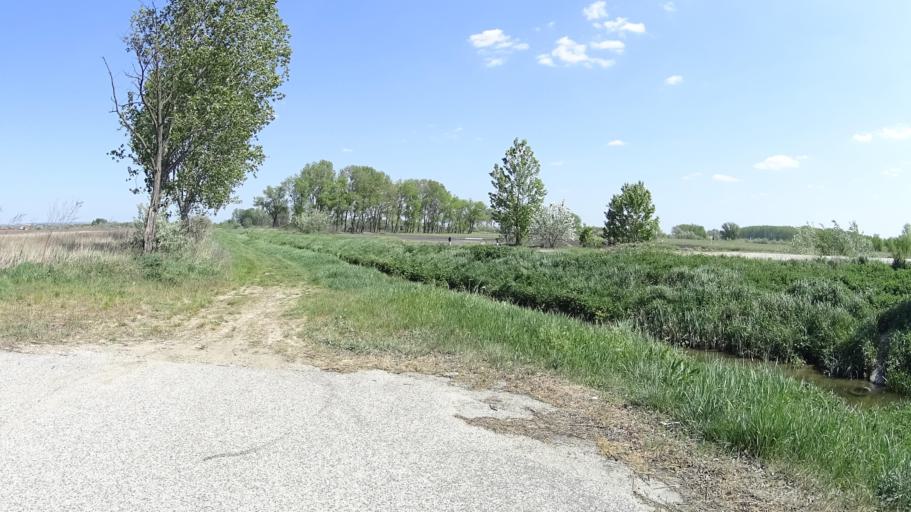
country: HU
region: Pest
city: Gyal
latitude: 47.3818
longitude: 19.2551
